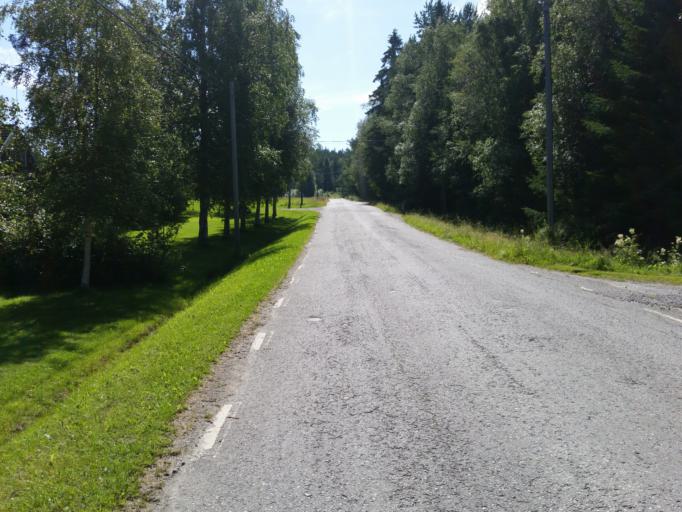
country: SE
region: Vaesterbotten
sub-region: Robertsfors Kommun
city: Robertsfors
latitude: 64.0419
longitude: 20.8579
